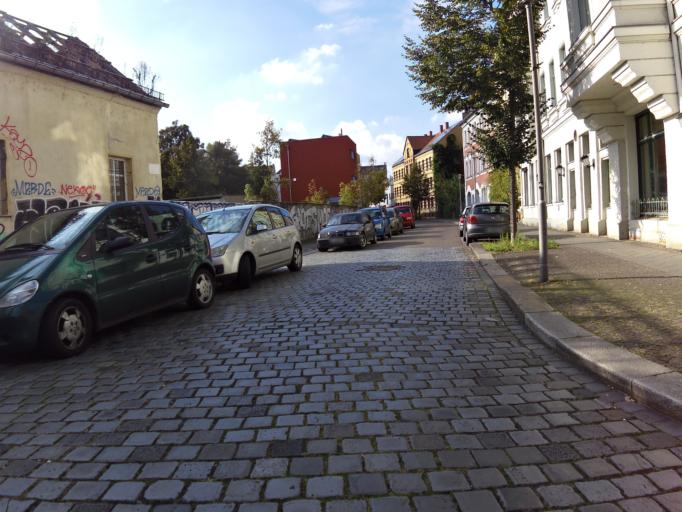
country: DE
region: Saxony
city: Leipzig
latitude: 51.3386
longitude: 12.3324
